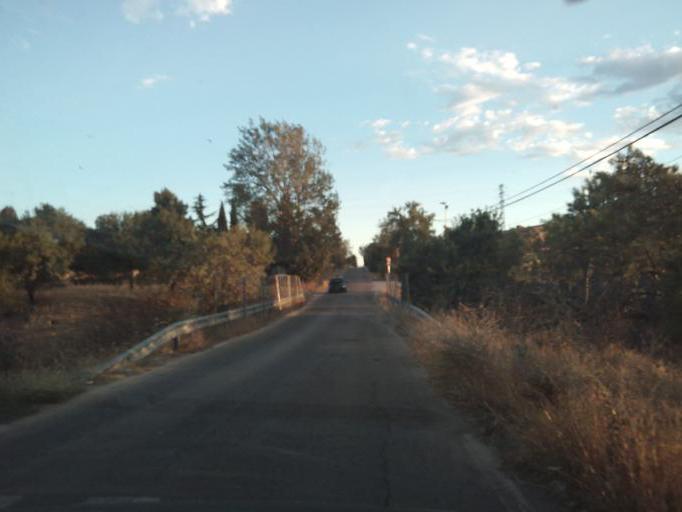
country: ES
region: Madrid
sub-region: Provincia de Madrid
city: Algete
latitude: 40.5959
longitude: -3.5063
